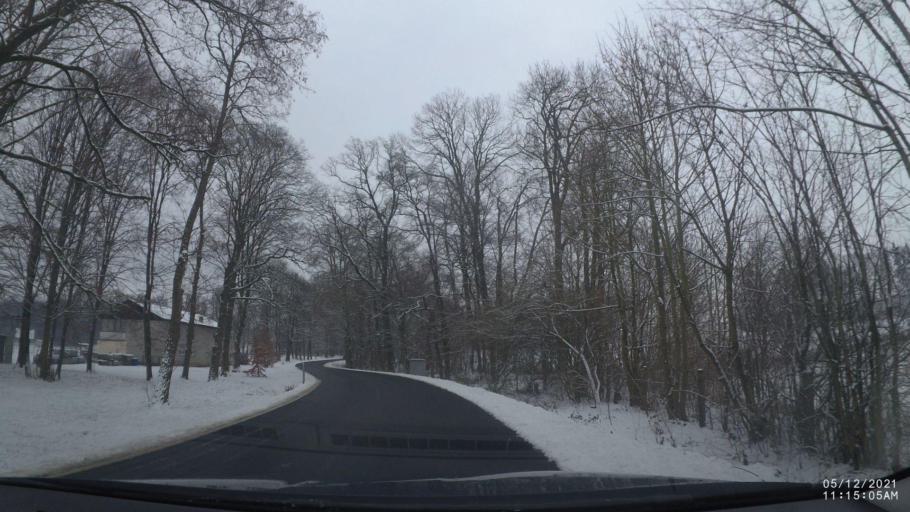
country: CZ
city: Solnice
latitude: 50.1866
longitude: 16.2146
